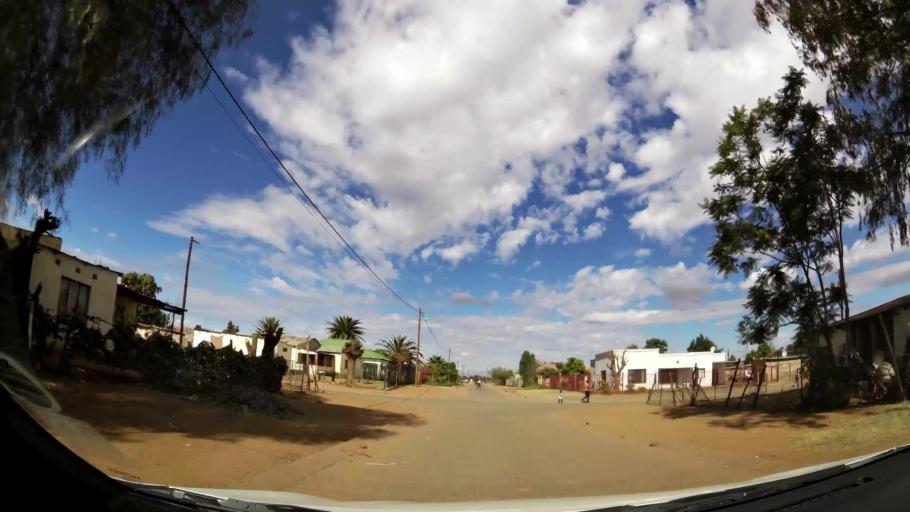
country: ZA
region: Limpopo
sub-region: Waterberg District Municipality
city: Bela-Bela
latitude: -24.8900
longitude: 28.3147
